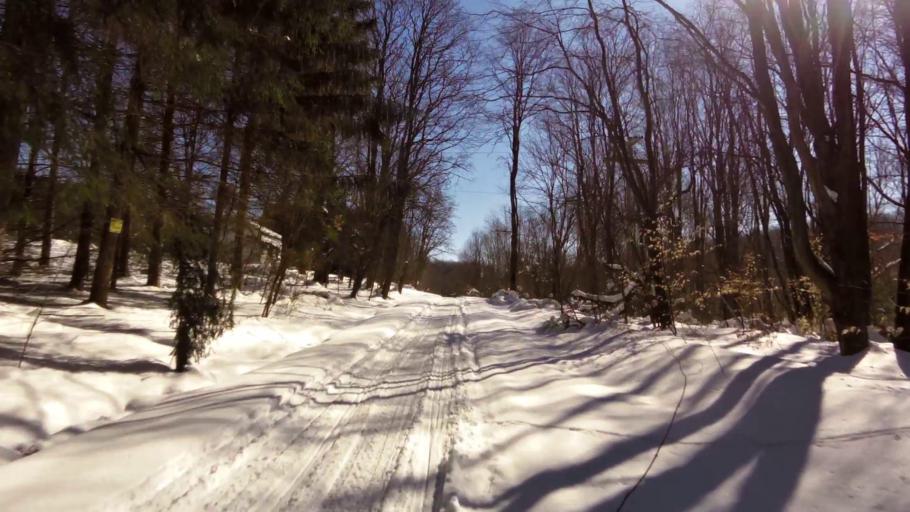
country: US
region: New York
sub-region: Allegany County
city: Cuba
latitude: 42.3052
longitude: -78.2695
